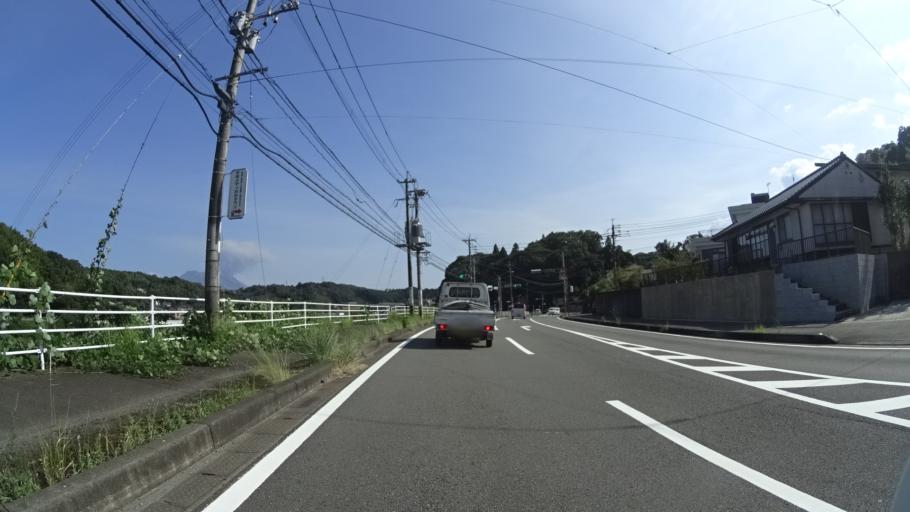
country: JP
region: Kagoshima
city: Kagoshima-shi
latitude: 31.6558
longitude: 130.5502
